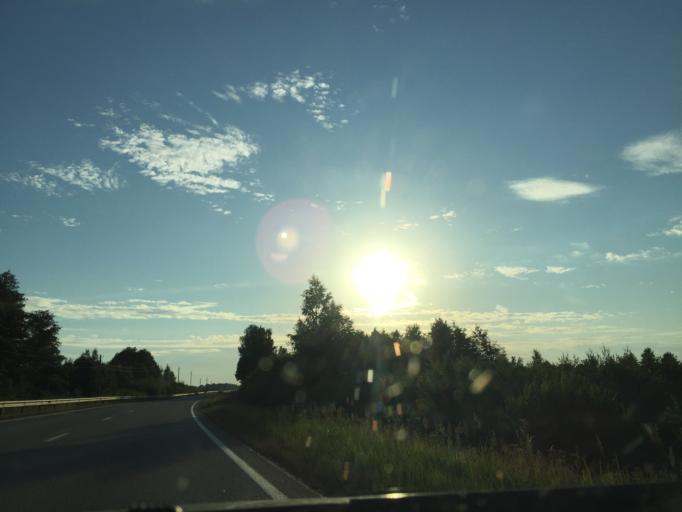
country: LV
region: Livani
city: Livani
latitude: 56.5348
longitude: 26.2935
